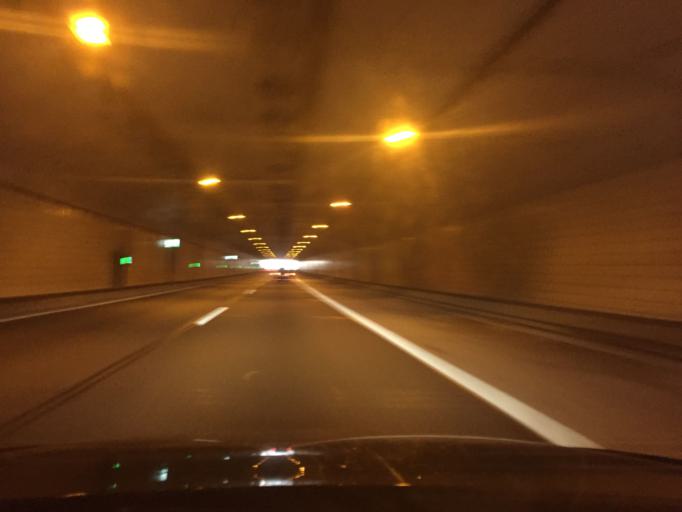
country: DE
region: Bavaria
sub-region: Upper Bavaria
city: Unterhaching
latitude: 48.0702
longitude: 11.6289
